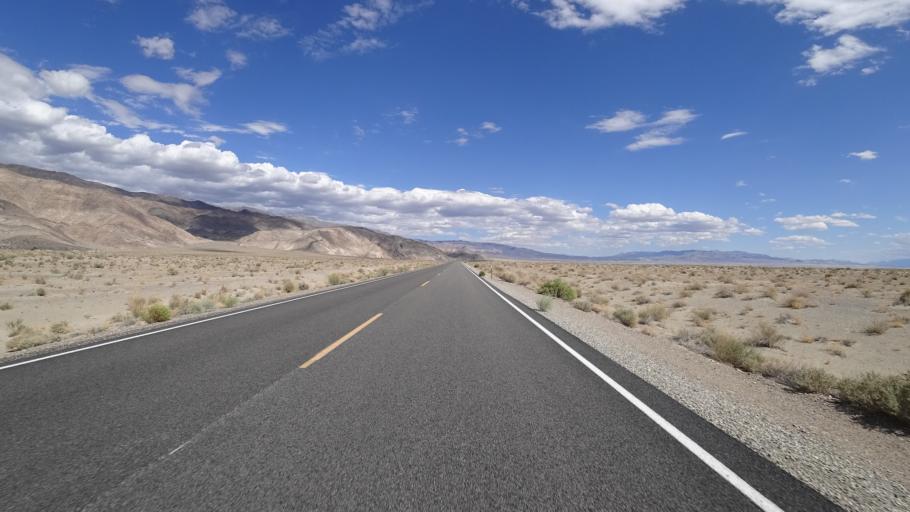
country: US
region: California
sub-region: Inyo County
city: Lone Pine
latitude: 36.5515
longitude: -117.9518
